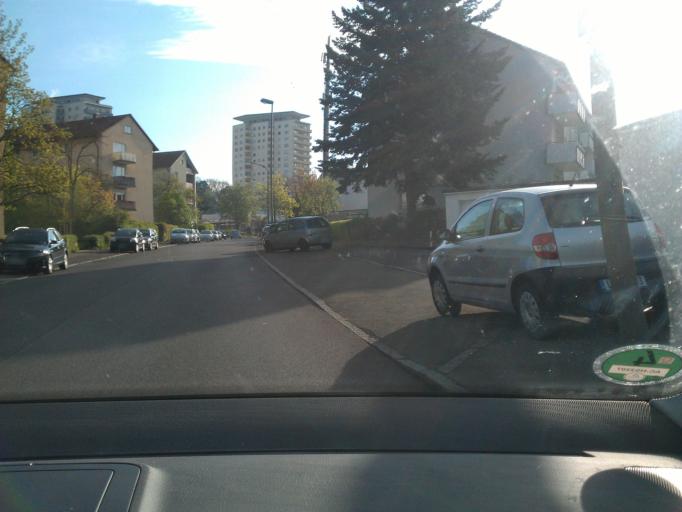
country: DE
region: Baden-Wuerttemberg
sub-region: Tuebingen Region
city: Ulm
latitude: 48.4077
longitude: 9.9574
